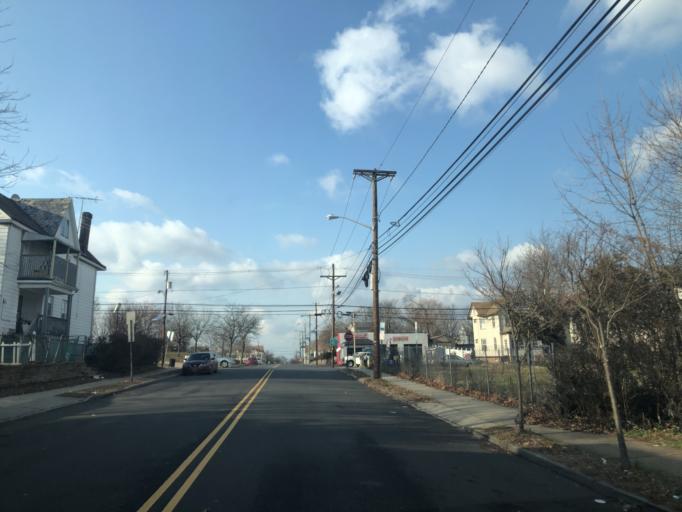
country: US
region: New Jersey
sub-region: Middlesex County
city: New Brunswick
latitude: 40.4840
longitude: -74.4423
